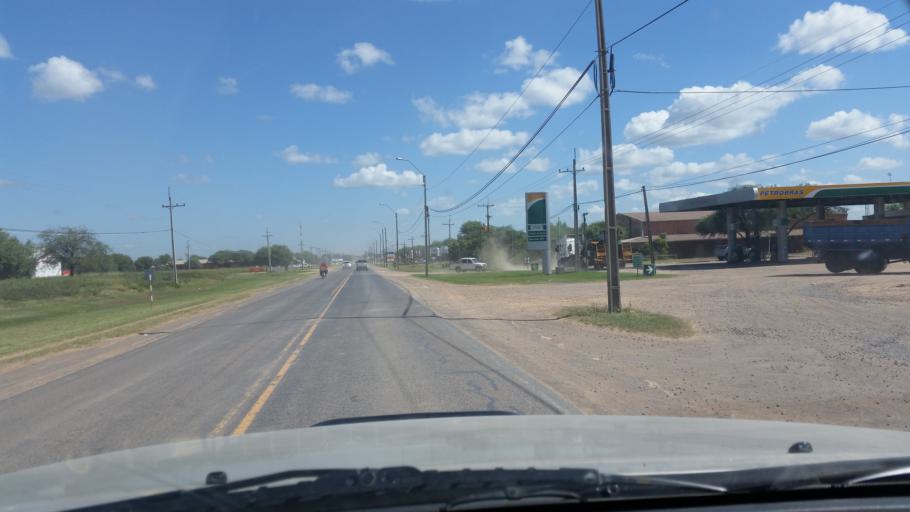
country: PY
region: Boqueron
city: Colonia Menno
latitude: -22.3950
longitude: -59.8365
